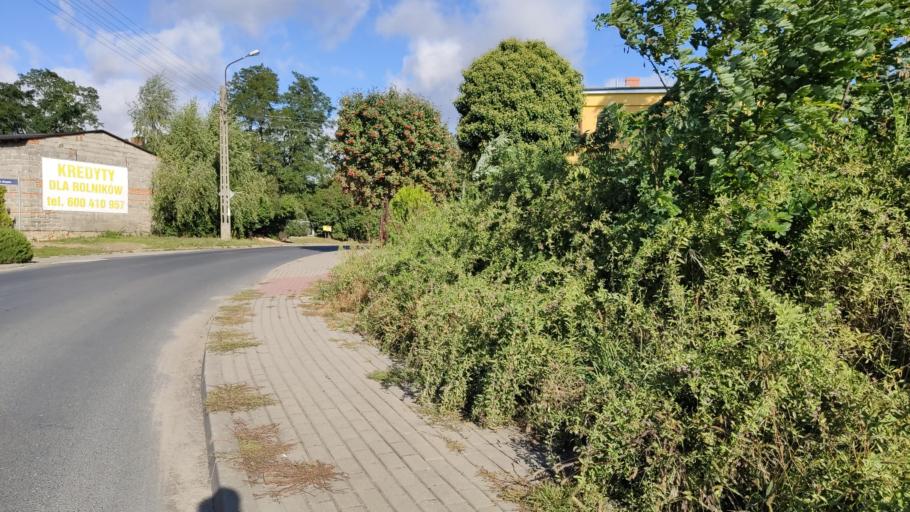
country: PL
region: Kujawsko-Pomorskie
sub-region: Powiat zninski
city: Znin
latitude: 52.8534
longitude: 17.7562
